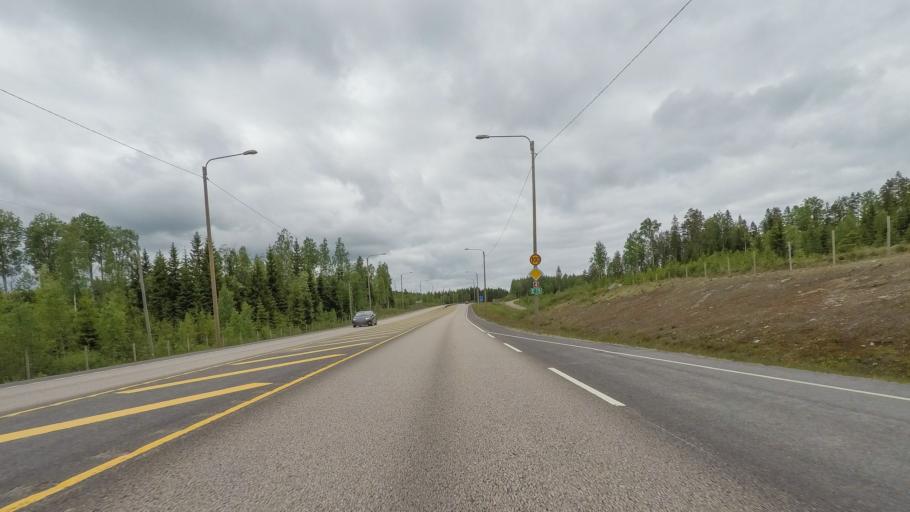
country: FI
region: Central Finland
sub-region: Jyvaeskylae
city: Toivakka
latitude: 62.0092
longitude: 26.0496
